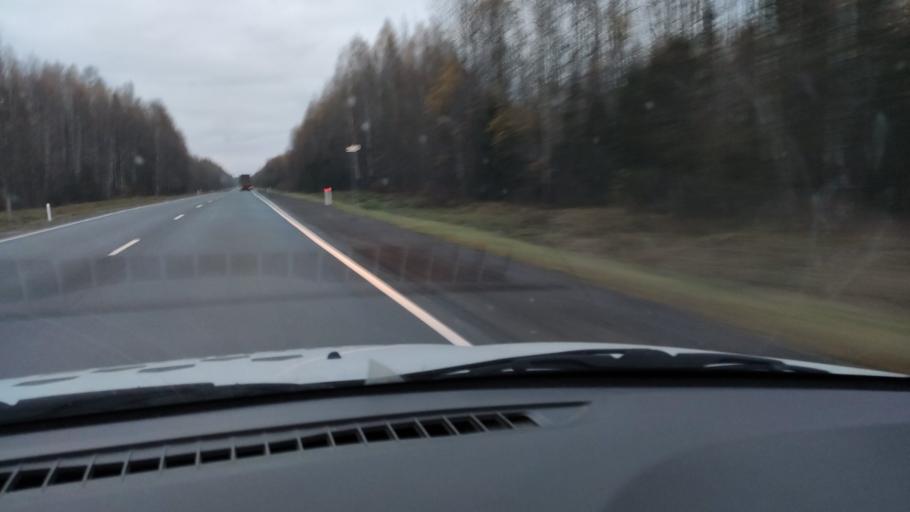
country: RU
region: Kirov
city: Kostino
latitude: 58.8337
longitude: 53.0363
